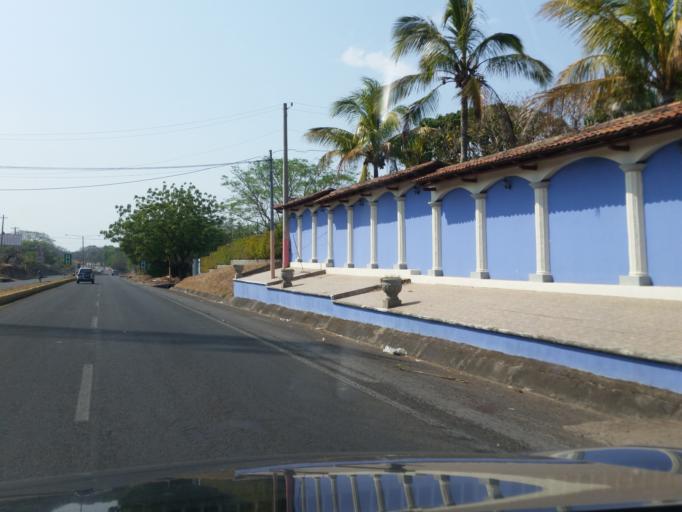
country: NI
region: Granada
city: Granada
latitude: 11.9569
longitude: -85.9905
